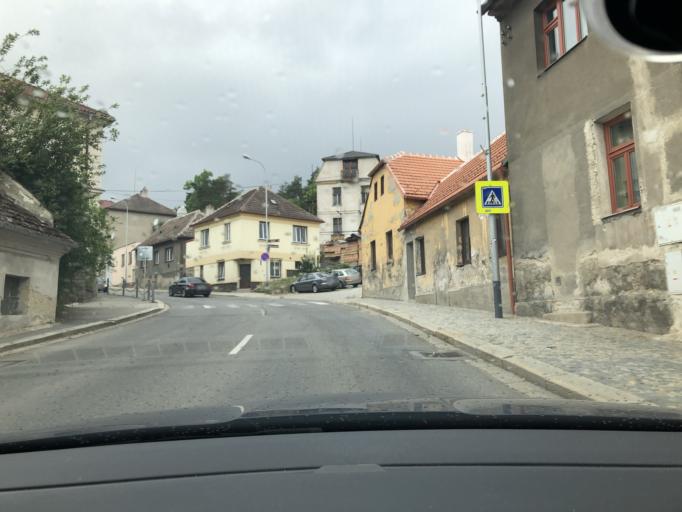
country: CZ
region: Vysocina
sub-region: Okres Trebic
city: Trebic
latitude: 49.2176
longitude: 15.8749
